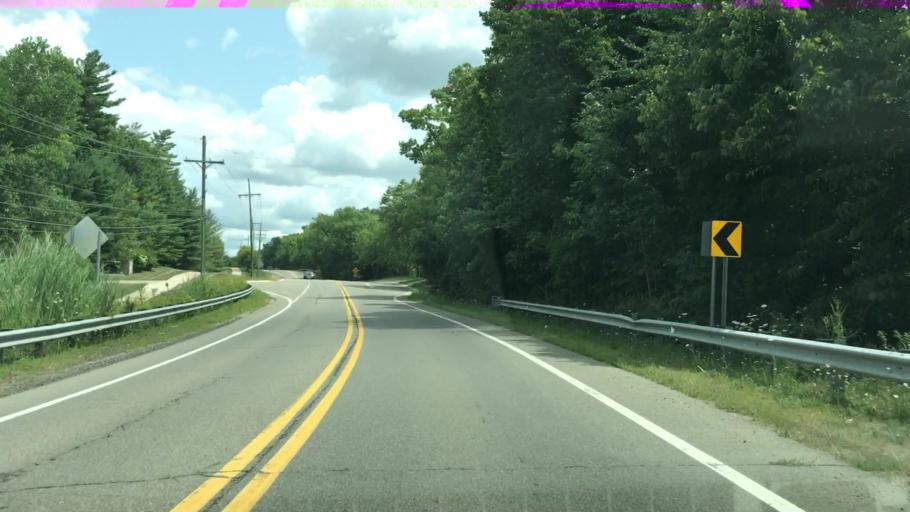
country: US
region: Michigan
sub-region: Oakland County
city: Rochester
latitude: 42.6854
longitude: -83.1067
